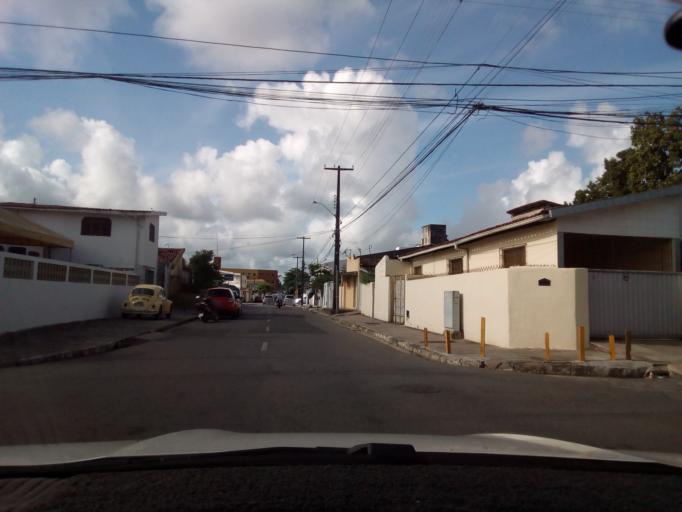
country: BR
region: Paraiba
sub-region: Joao Pessoa
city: Joao Pessoa
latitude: -7.1326
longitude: -34.8750
